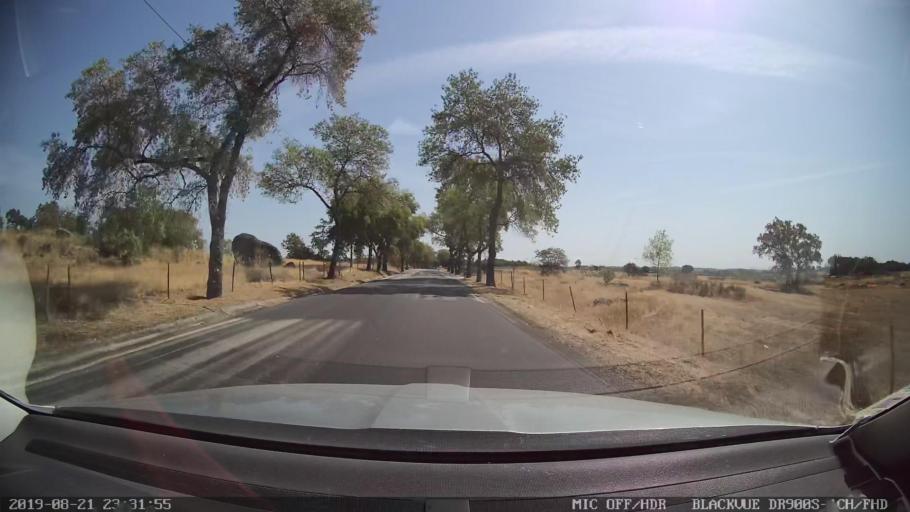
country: PT
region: Guarda
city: Alcains
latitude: 39.8753
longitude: -7.4217
